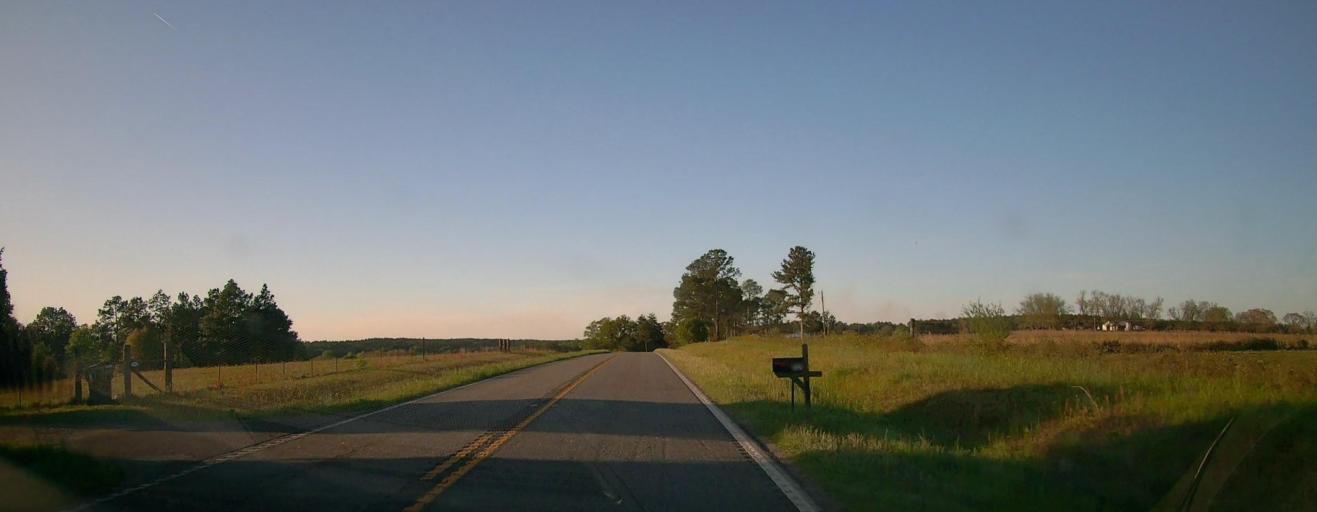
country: US
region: Georgia
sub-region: Marion County
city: Buena Vista
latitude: 32.3960
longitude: -84.4431
